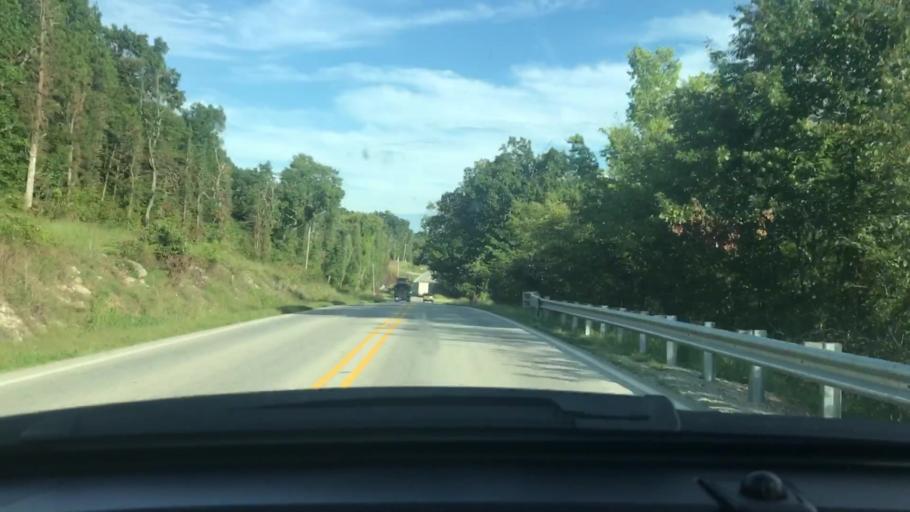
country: US
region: Arkansas
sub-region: Sharp County
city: Cherokee Village
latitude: 36.3088
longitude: -91.4580
